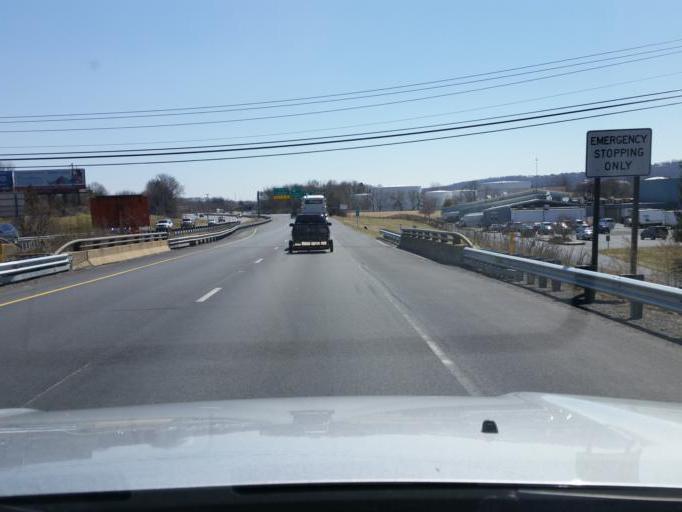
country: US
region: Pennsylvania
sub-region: Dauphin County
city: Highspire
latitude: 40.2263
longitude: -76.7928
